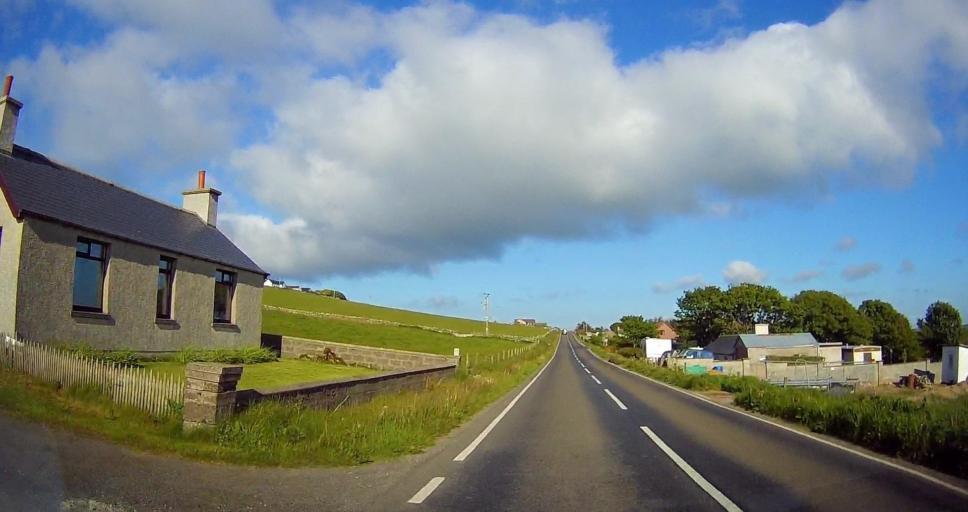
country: GB
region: Scotland
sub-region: Orkney Islands
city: Orkney
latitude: 58.9789
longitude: -3.0205
